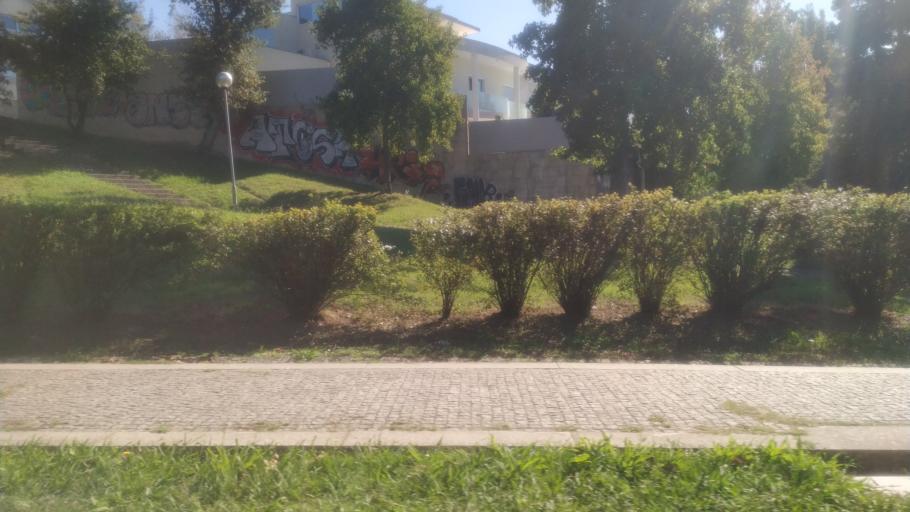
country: PT
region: Porto
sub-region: Matosinhos
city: Senhora da Hora
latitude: 41.1800
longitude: -8.6669
